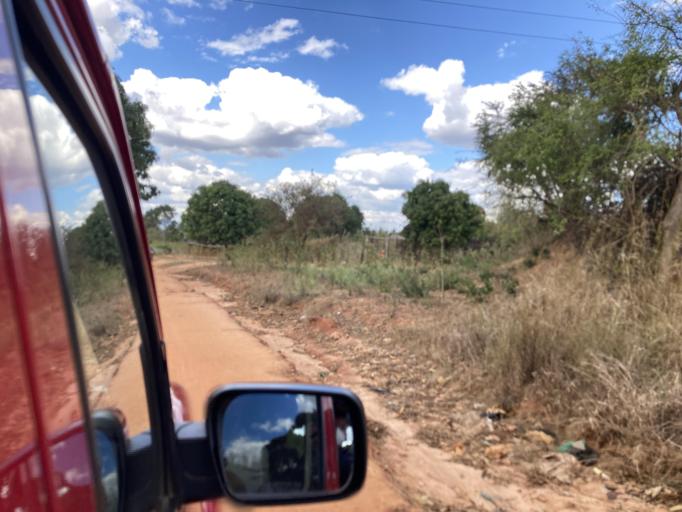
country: MZ
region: Cabo Delgado
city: Montepuez
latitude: -13.1267
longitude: 39.0339
